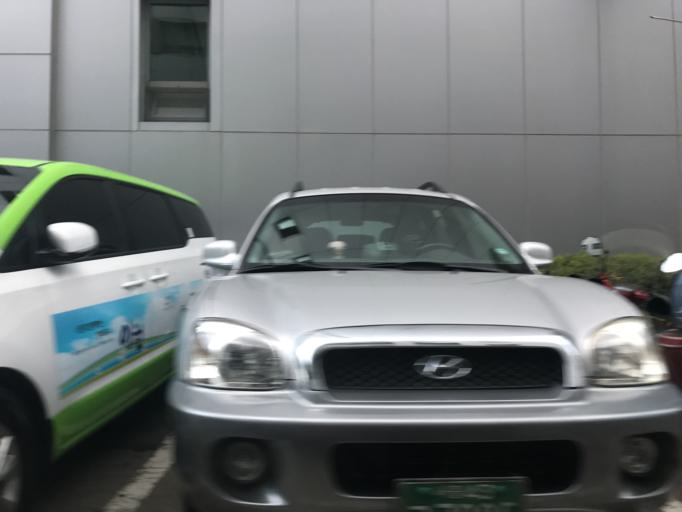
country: KR
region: Seoul
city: Seoul
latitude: 37.5628
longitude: 126.9399
